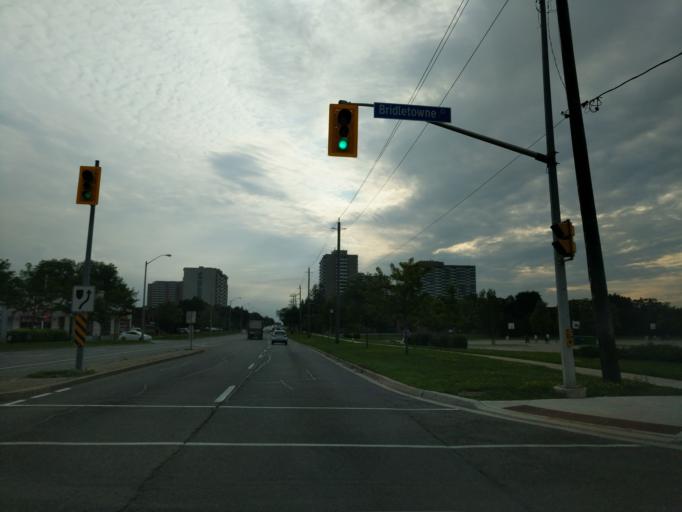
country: CA
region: Ontario
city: Scarborough
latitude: 43.7959
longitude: -79.3194
